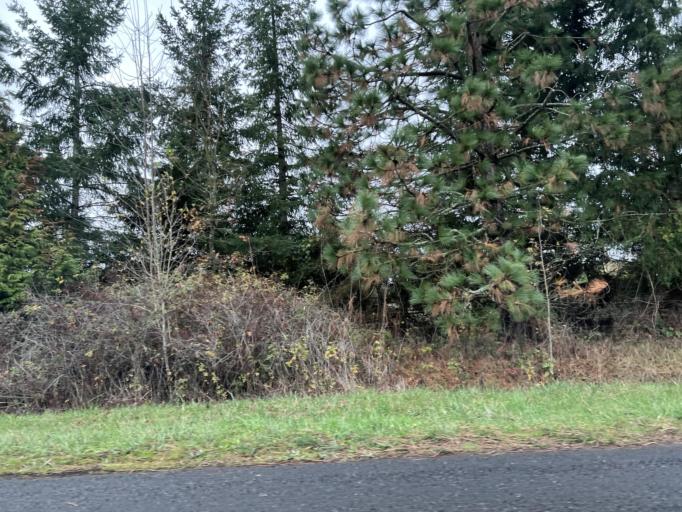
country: US
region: Oregon
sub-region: Polk County
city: Independence
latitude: 44.8102
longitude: -123.0858
